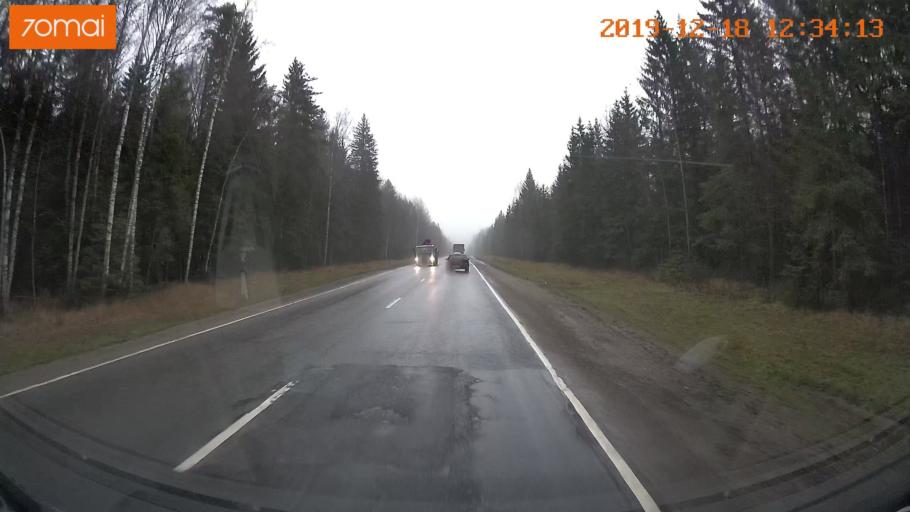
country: RU
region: Moskovskaya
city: Rumyantsevo
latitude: 56.1192
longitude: 36.5695
